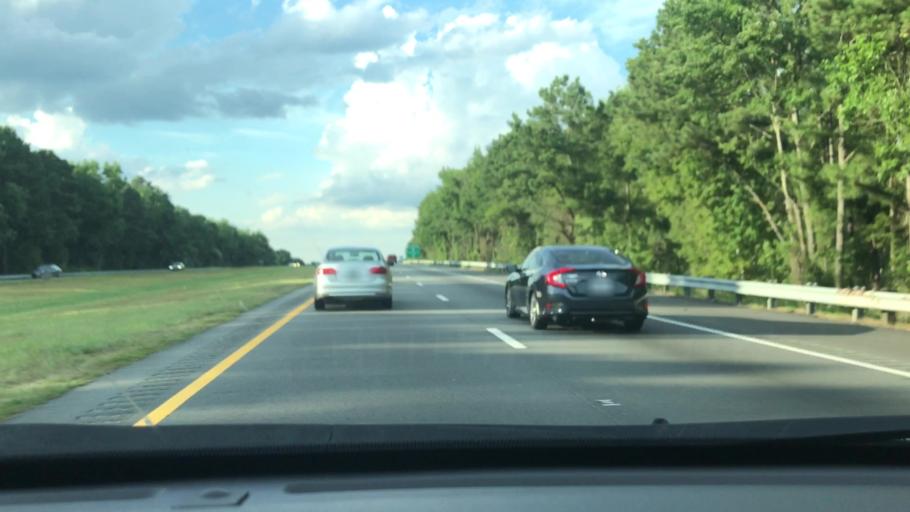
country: US
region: North Carolina
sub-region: Cumberland County
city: Vander
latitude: 35.0308
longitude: -78.8068
